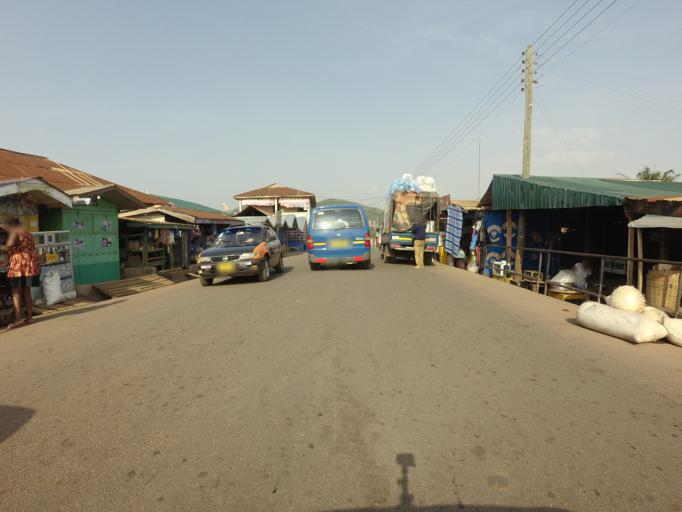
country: GH
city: Akropong
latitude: 6.1552
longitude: 0.0235
